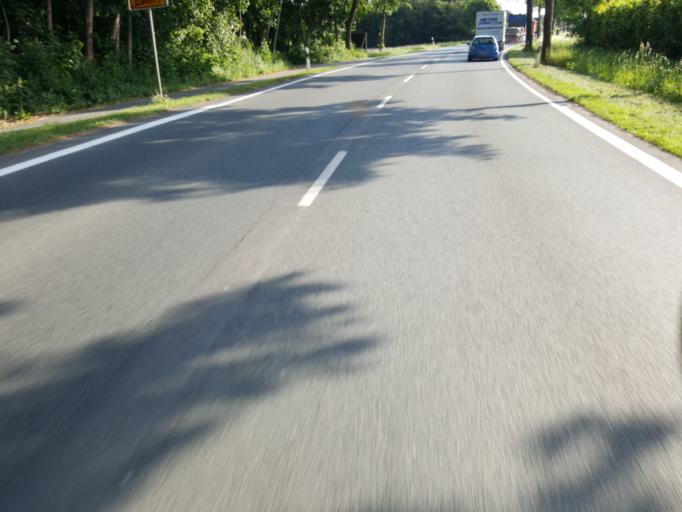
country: DE
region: Lower Saxony
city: Estorf
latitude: 52.5907
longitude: 9.1438
